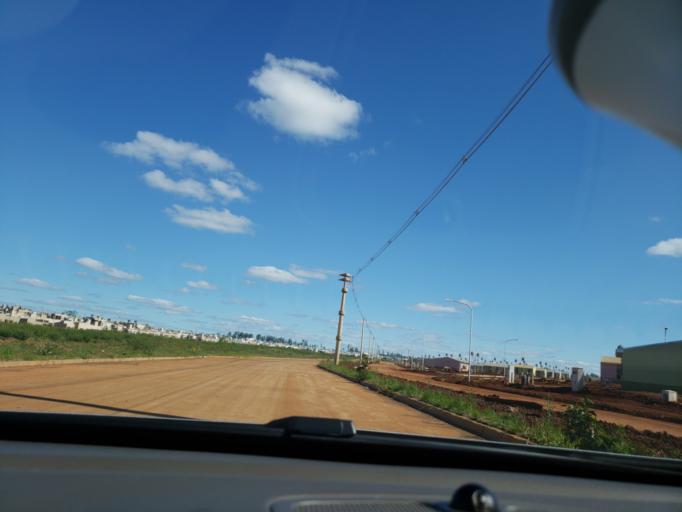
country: AR
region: Misiones
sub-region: Departamento de Capital
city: Posadas
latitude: -27.3994
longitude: -55.9895
